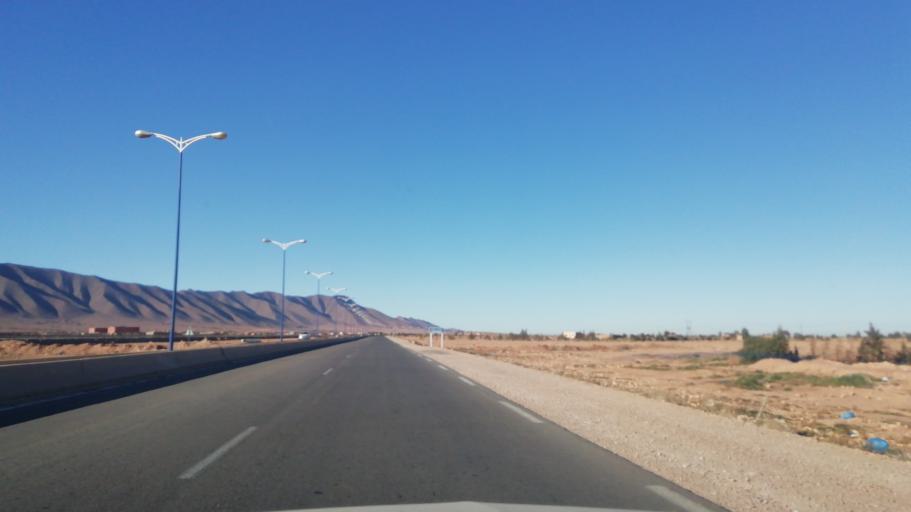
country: DZ
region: Wilaya de Naama
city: Naama
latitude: 33.5630
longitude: -0.2382
